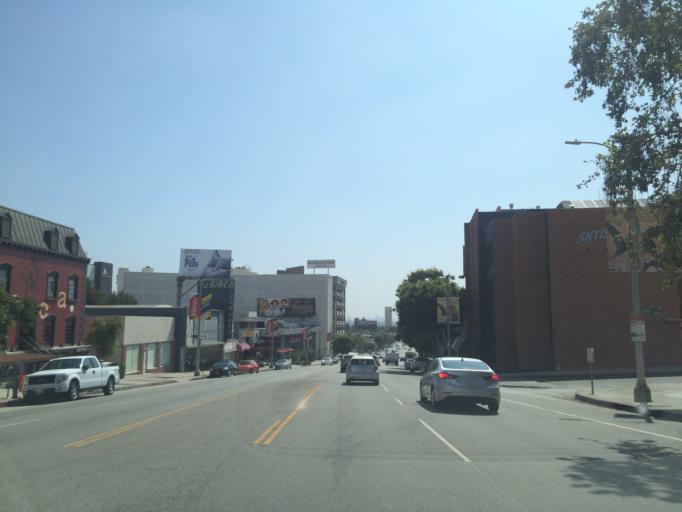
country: US
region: California
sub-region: Los Angeles County
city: Beverly Hills
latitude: 34.0552
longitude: -118.3980
